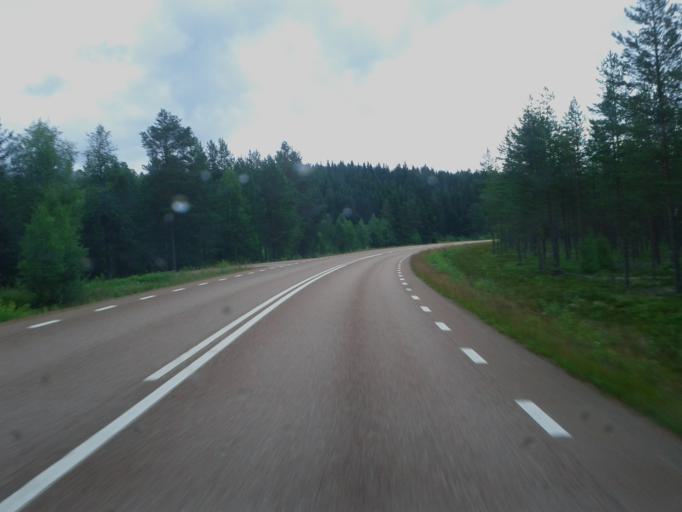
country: SE
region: Dalarna
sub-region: Alvdalens Kommun
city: AElvdalen
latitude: 61.2794
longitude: 13.9343
